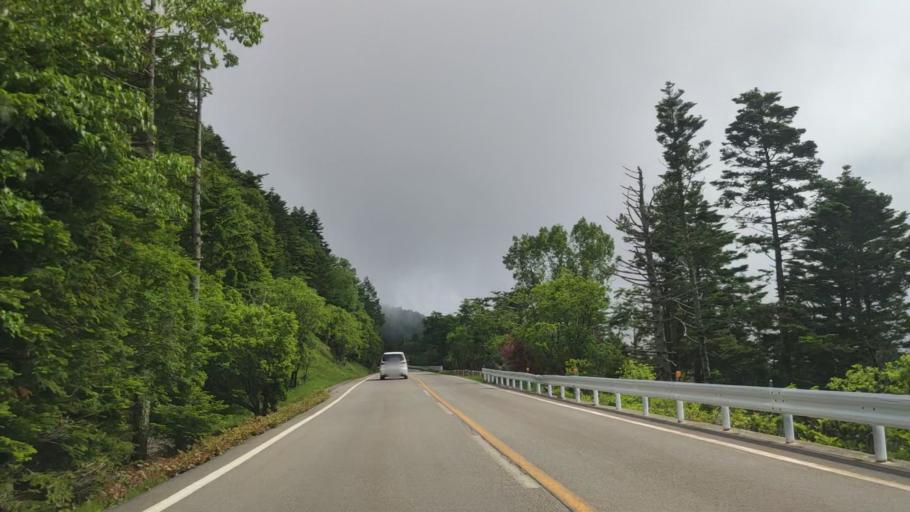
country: JP
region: Yamanashi
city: Fujikawaguchiko
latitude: 35.3979
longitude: 138.6921
